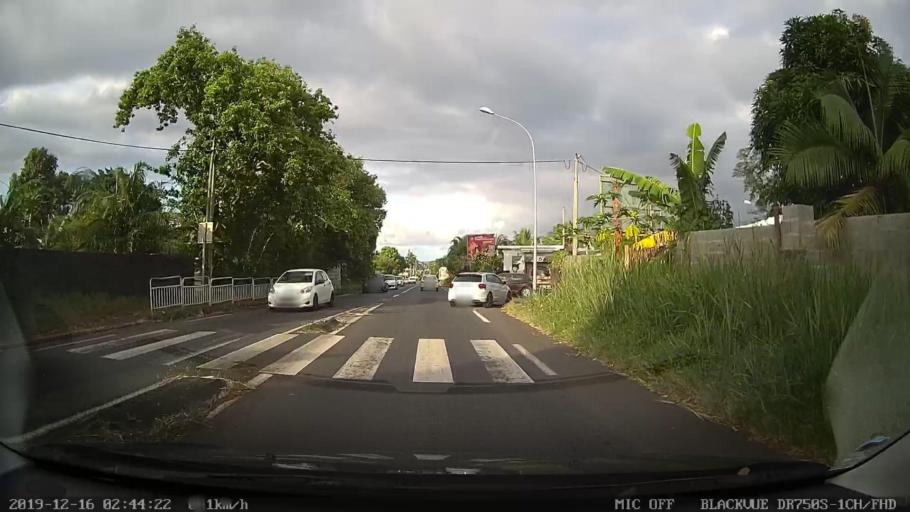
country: RE
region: Reunion
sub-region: Reunion
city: Saint-Benoit
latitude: -21.0501
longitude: 55.7161
